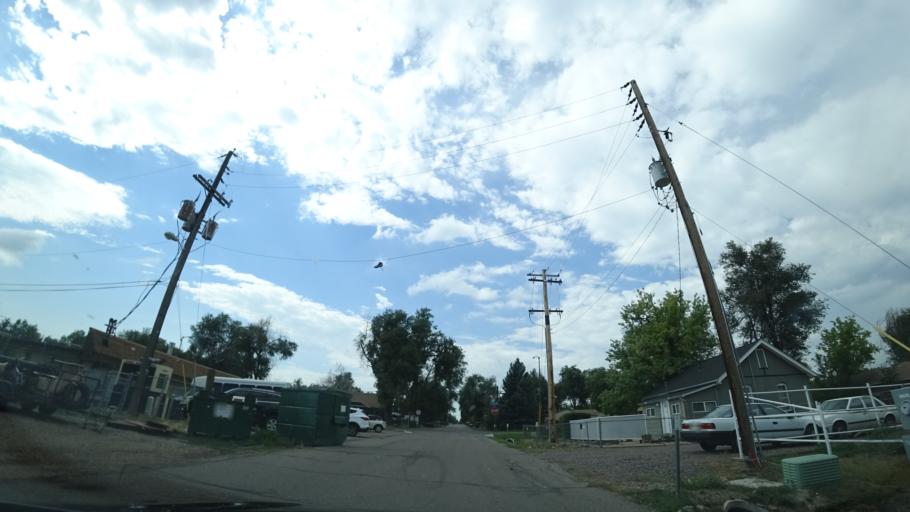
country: US
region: Colorado
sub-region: Jefferson County
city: Lakewood
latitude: 39.7192
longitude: -105.0651
